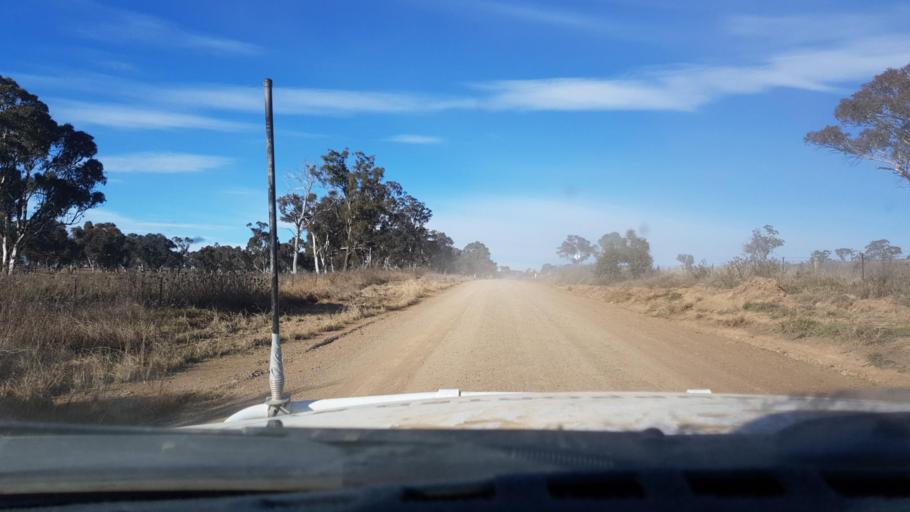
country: AU
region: New South Wales
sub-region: Armidale Dumaresq
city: Enmore
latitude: -30.7124
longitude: 151.5899
